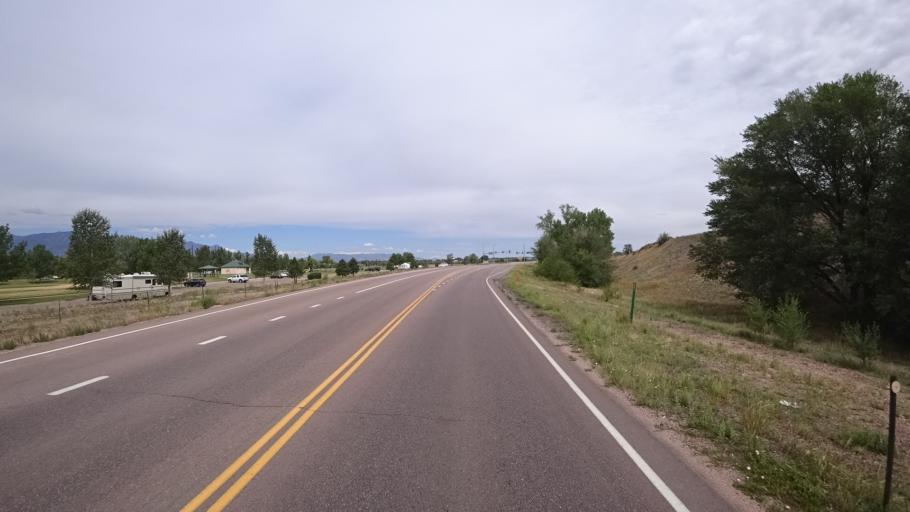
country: US
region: Colorado
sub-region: El Paso County
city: Fountain
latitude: 38.7073
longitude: -104.7112
